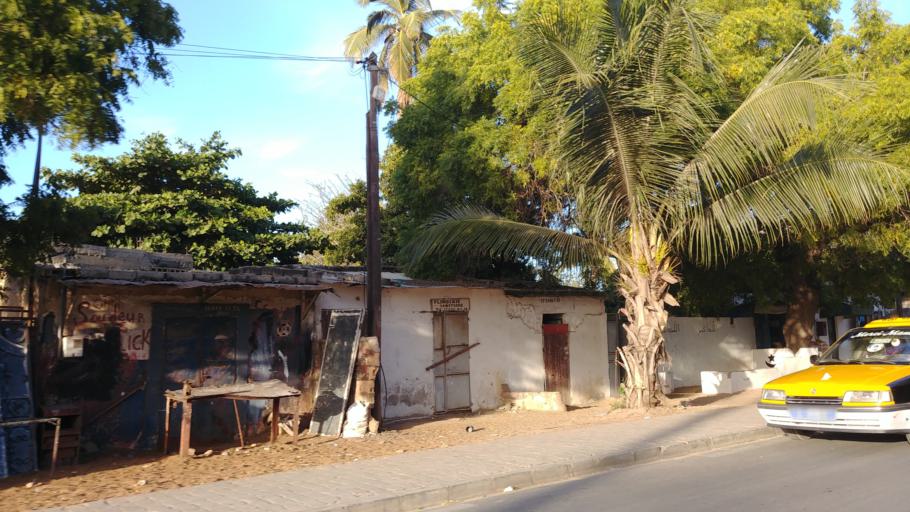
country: SN
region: Saint-Louis
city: Saint-Louis
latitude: 16.0255
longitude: -16.4874
